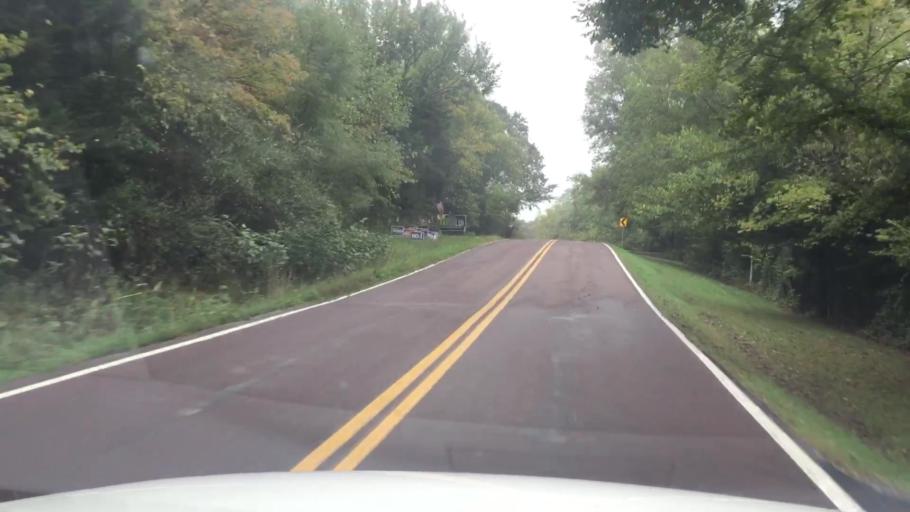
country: US
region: Missouri
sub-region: Boone County
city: Ashland
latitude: 38.8312
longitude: -92.3507
